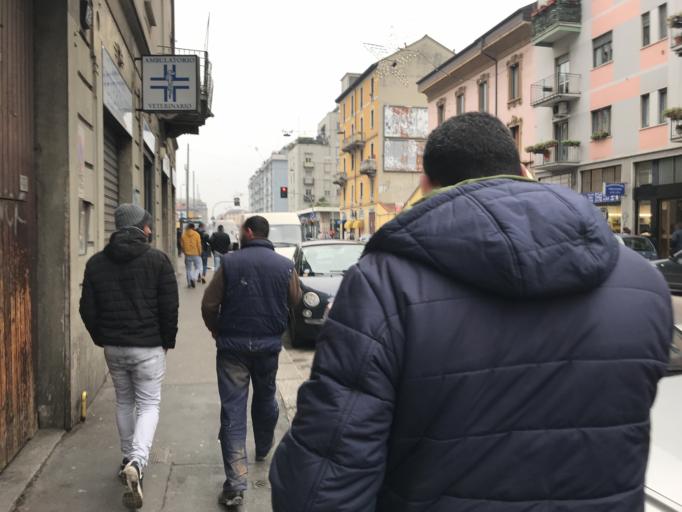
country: IT
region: Lombardy
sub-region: Citta metropolitana di Milano
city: Sesto San Giovanni
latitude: 45.4978
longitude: 9.2322
